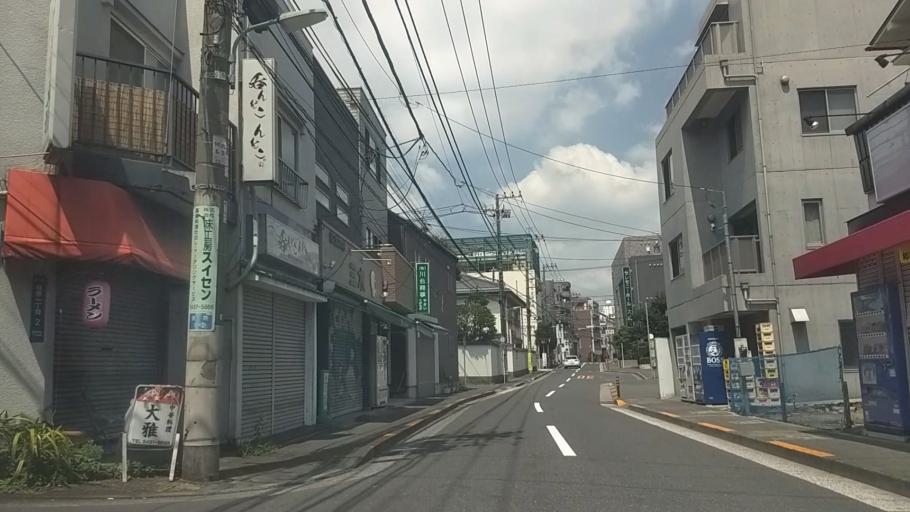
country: JP
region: Tokyo
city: Tokyo
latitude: 35.6216
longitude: 139.7137
